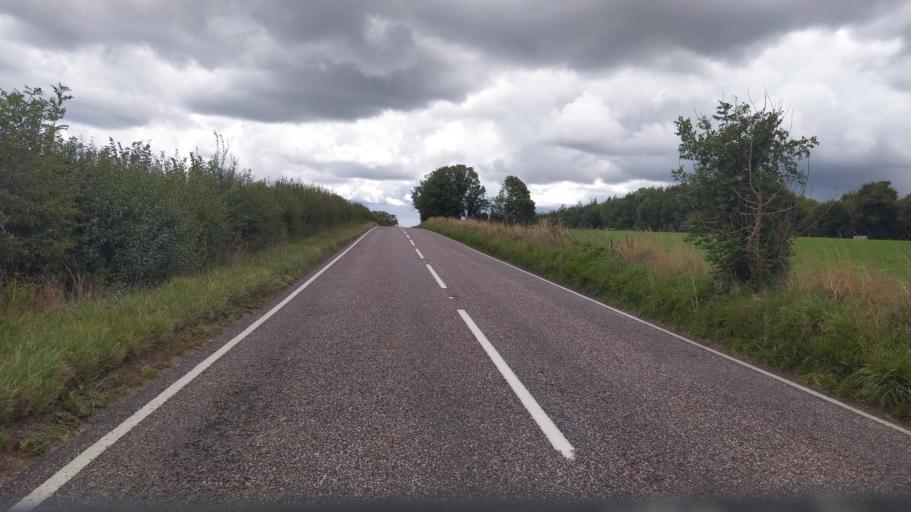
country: GB
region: England
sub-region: Wiltshire
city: Bower Chalke
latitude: 50.9296
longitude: -1.9545
